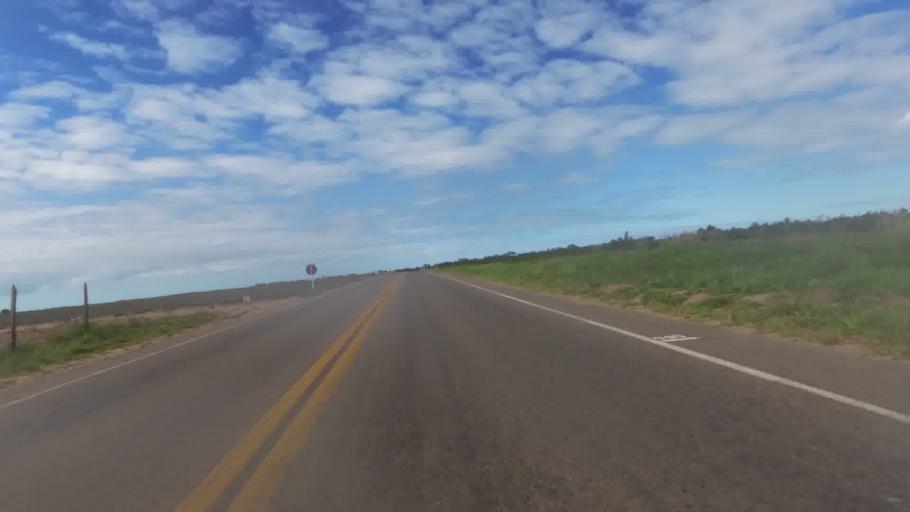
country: BR
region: Espirito Santo
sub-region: Marataizes
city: Marataizes
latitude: -21.0733
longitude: -40.8517
